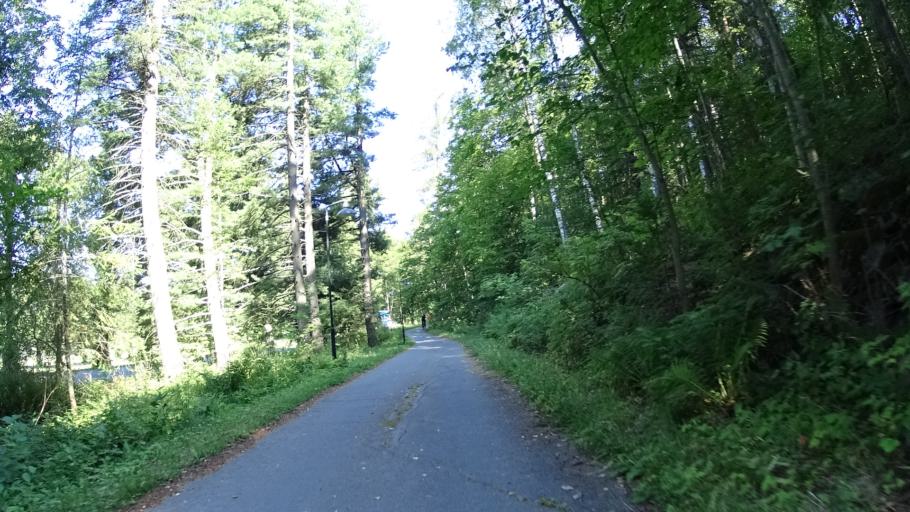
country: FI
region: Haeme
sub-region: Haemeenlinna
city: Haemeenlinna
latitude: 61.0242
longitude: 24.4461
